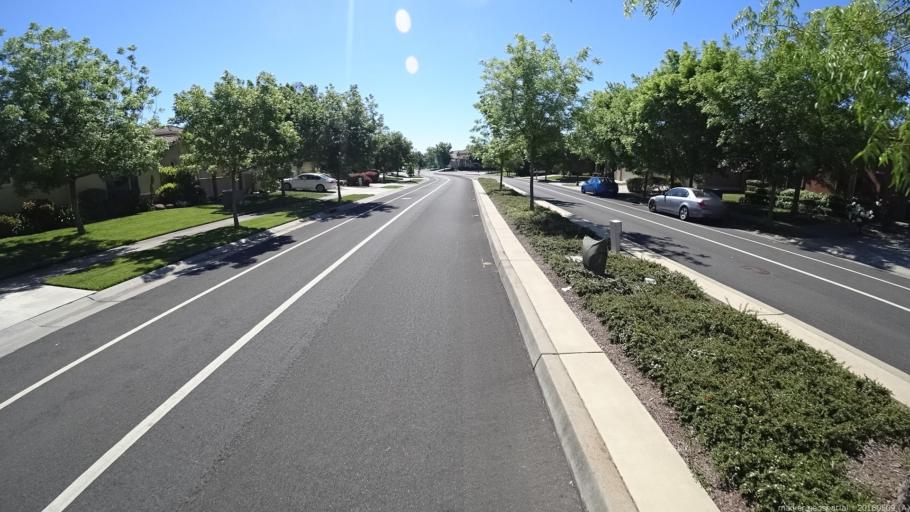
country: US
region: California
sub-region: Sacramento County
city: Elverta
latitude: 38.6785
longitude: -121.5206
